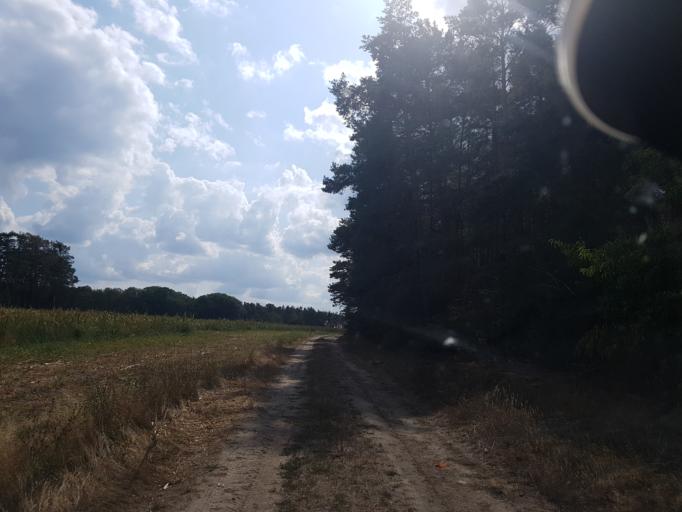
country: DE
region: Brandenburg
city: Calau
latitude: 51.7669
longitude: 13.9657
